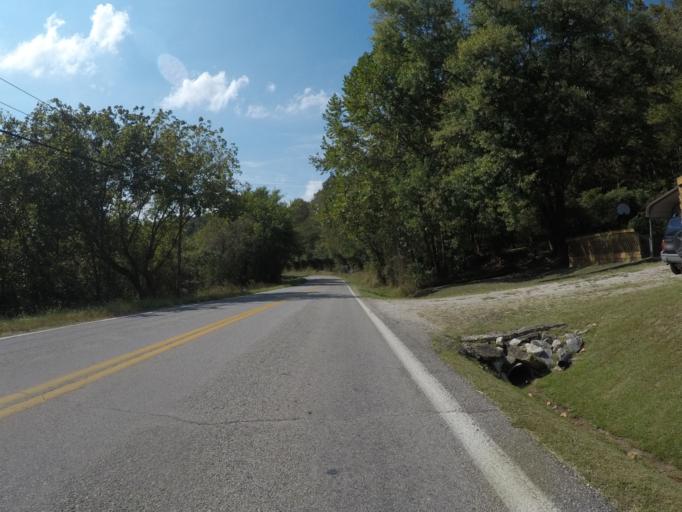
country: US
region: West Virginia
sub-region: Cabell County
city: Lesage
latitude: 38.5487
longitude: -82.3922
